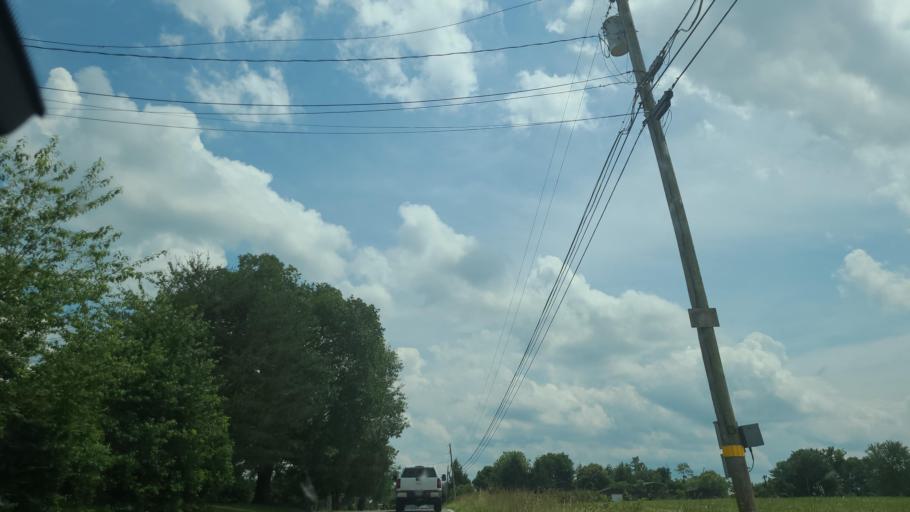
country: US
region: Tennessee
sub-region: Cumberland County
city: Lake Tansi
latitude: 35.9060
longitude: -85.0283
